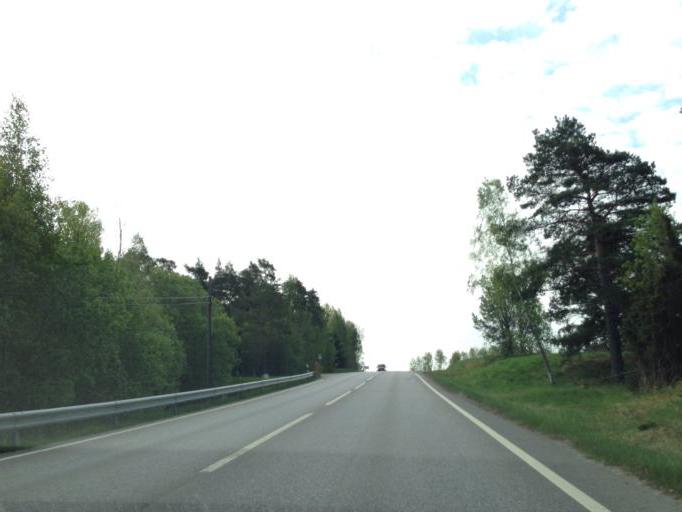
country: SE
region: Soedermanland
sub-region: Flens Kommun
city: Malmkoping
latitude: 59.1151
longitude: 16.7618
